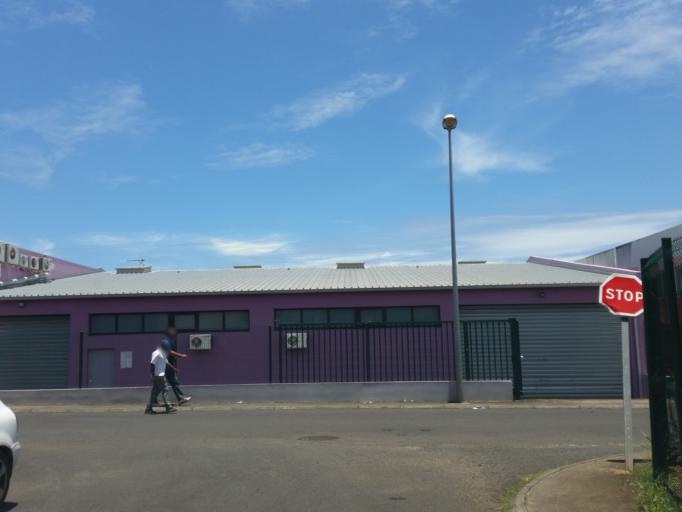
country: RE
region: Reunion
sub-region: Reunion
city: Sainte-Marie
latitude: -20.8999
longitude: 55.5339
